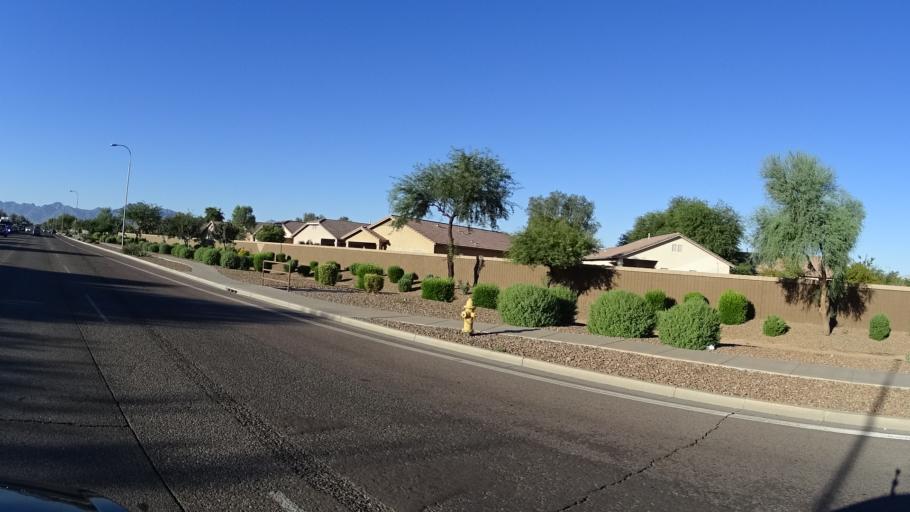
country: US
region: Arizona
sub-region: Maricopa County
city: Tolleson
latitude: 33.4349
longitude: -112.2384
